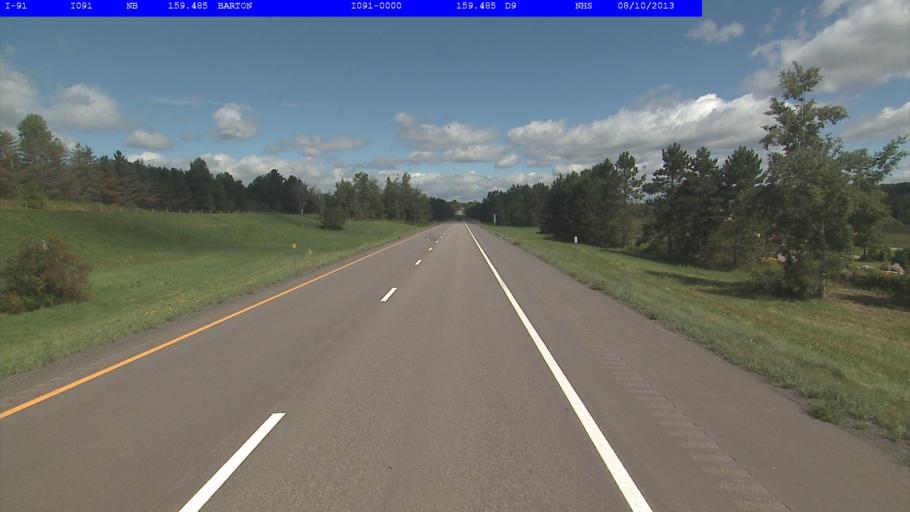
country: US
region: Vermont
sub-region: Orleans County
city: Newport
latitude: 44.7790
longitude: -72.2148
